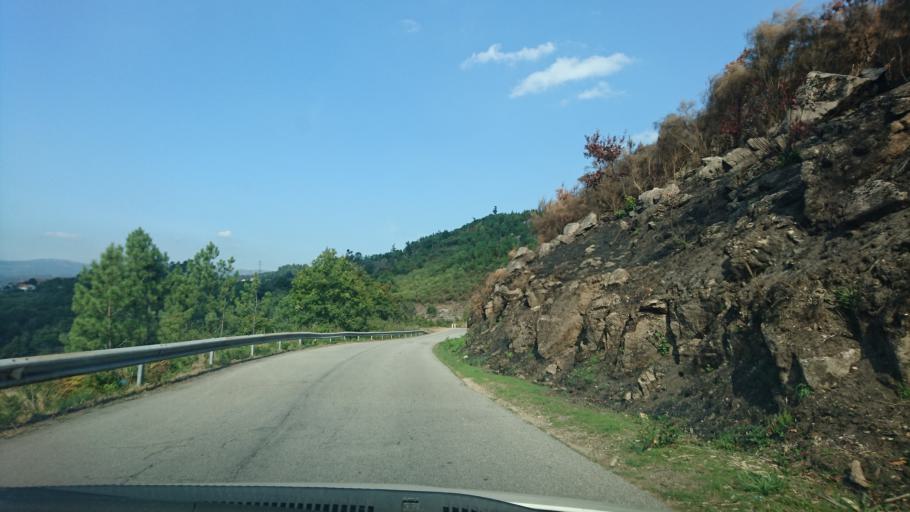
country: PT
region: Vila Real
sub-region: Mondim de Basto
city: Mondim de Basto
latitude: 41.4490
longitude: -7.9243
